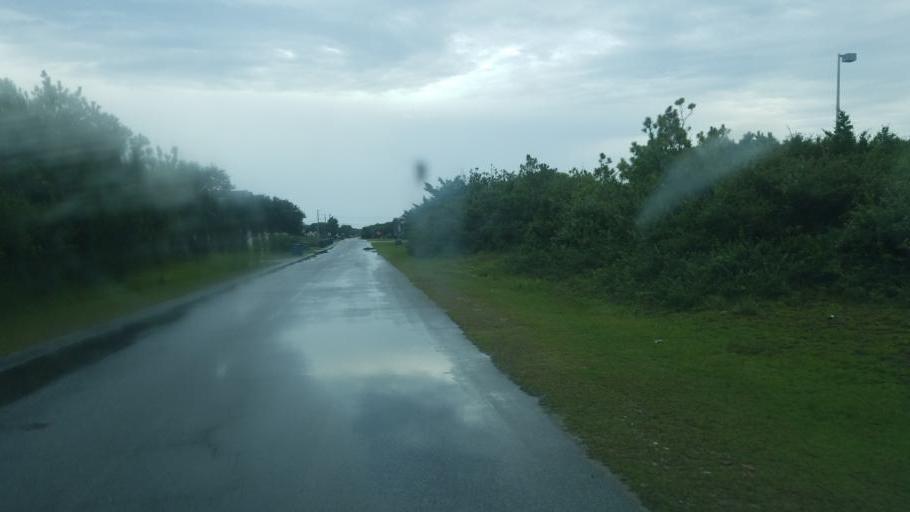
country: US
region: North Carolina
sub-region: Dare County
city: Nags Head
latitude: 35.9840
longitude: -75.6421
